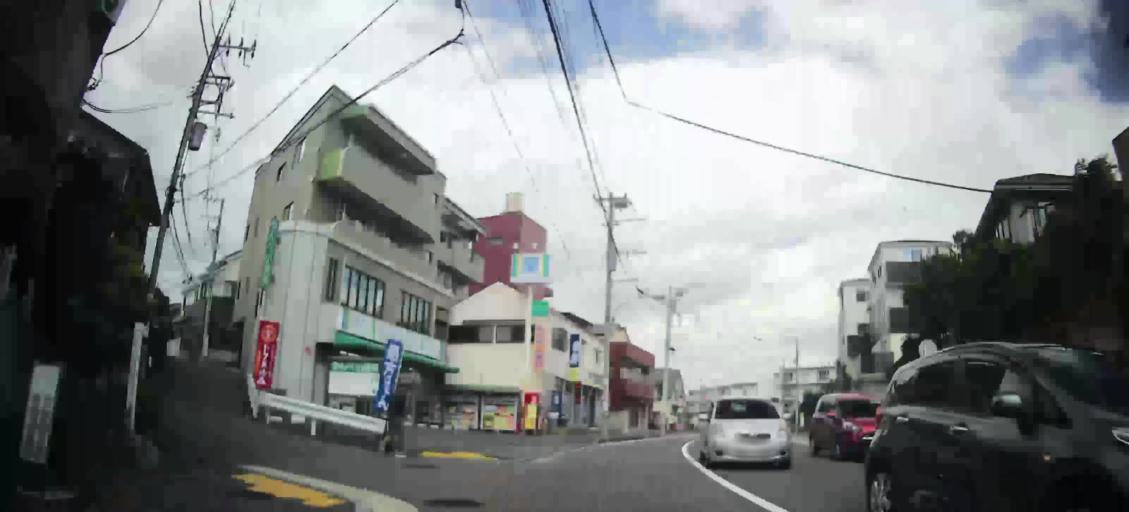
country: JP
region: Kanagawa
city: Minami-rinkan
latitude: 35.4790
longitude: 139.5485
